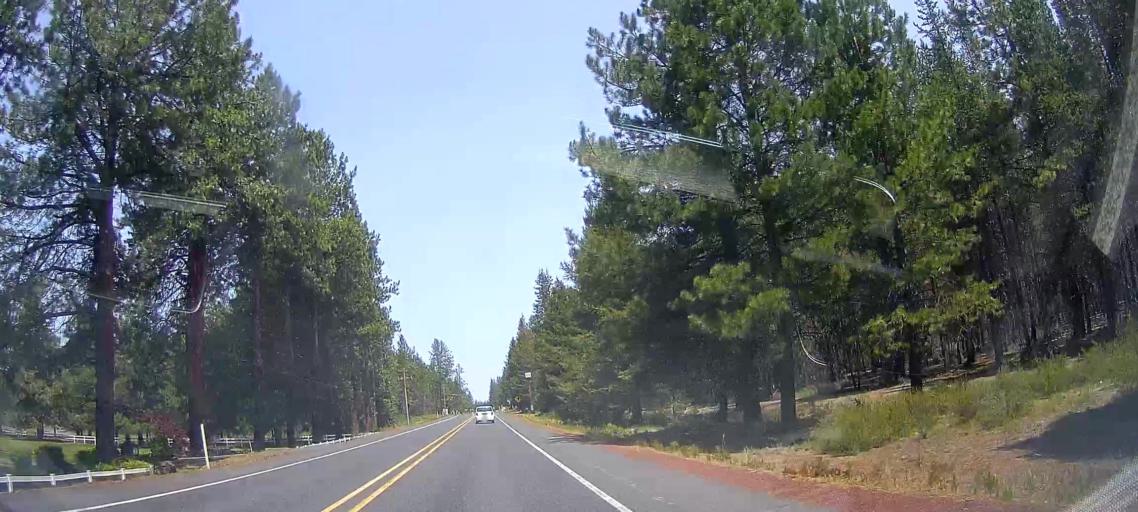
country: US
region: Oregon
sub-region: Deschutes County
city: La Pine
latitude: 43.4741
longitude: -121.6891
